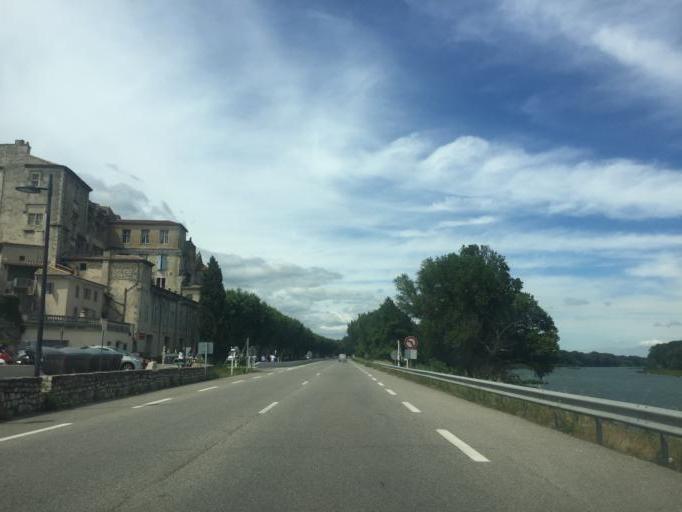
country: FR
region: Rhone-Alpes
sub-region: Departement de l'Ardeche
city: Bourg-Saint-Andeol
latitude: 44.3717
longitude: 4.6480
